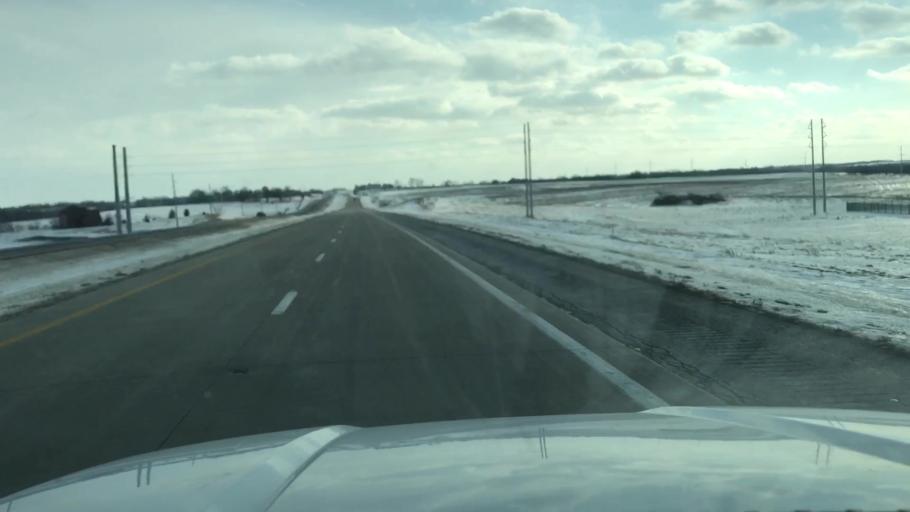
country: US
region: Missouri
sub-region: Nodaway County
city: Maryville
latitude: 40.2282
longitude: -94.8682
